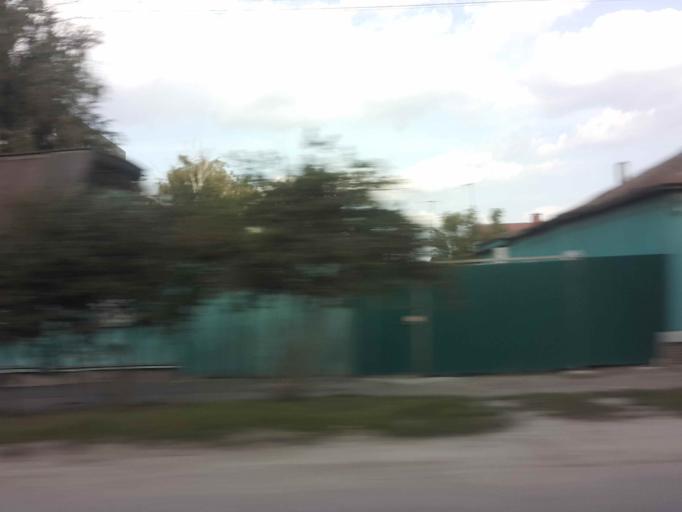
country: RU
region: Tambov
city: Tambov
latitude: 52.7171
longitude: 41.4388
